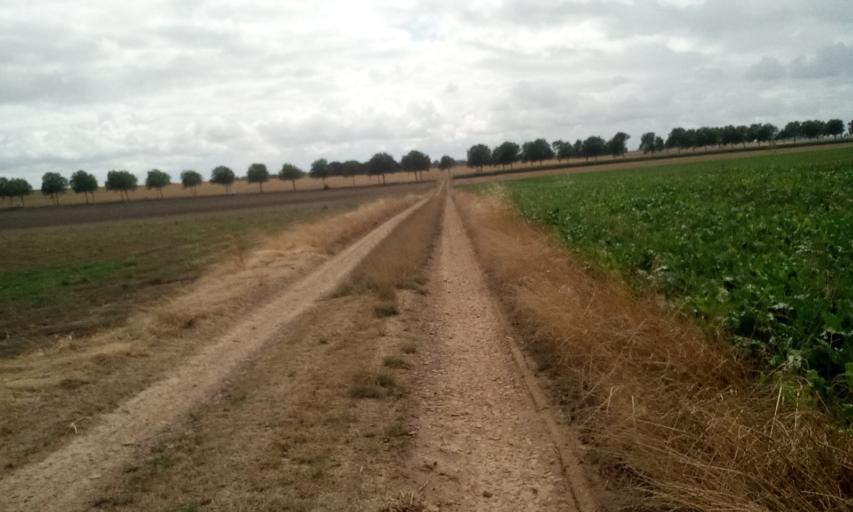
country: FR
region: Lower Normandy
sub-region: Departement du Calvados
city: Cheux
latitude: 49.1770
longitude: -0.5431
